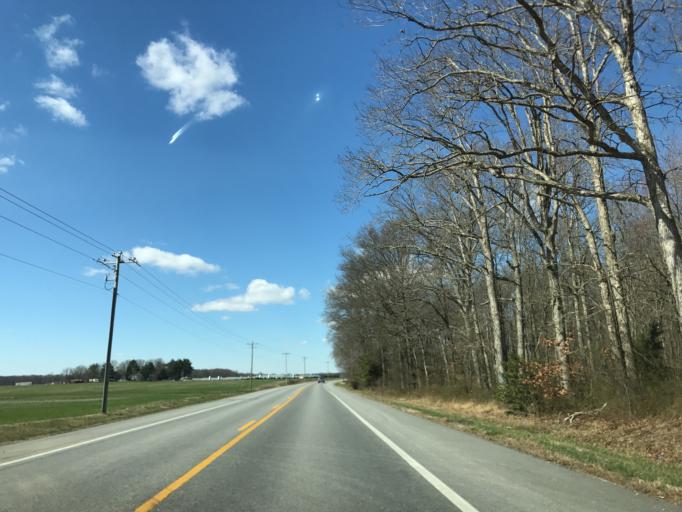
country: US
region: Maryland
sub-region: Caroline County
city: Greensboro
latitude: 39.0988
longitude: -75.8876
